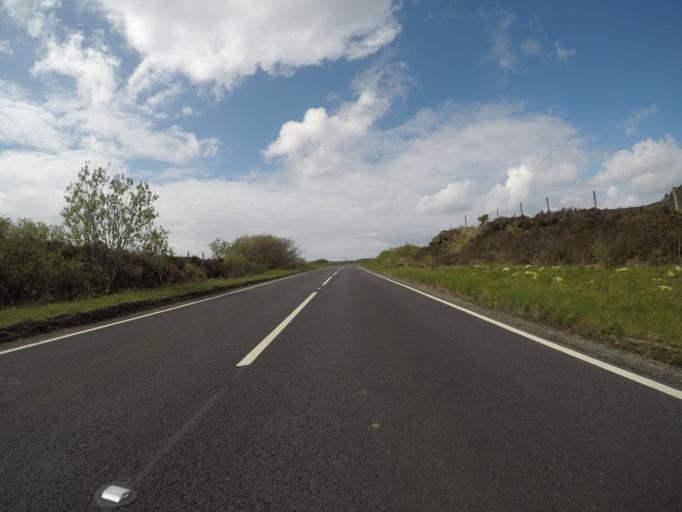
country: GB
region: Scotland
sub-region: Highland
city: Portree
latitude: 57.5341
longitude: -6.3584
